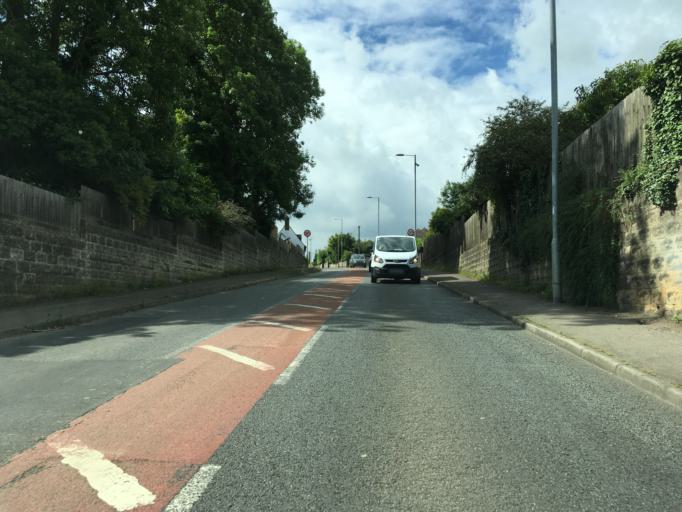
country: GB
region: England
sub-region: Borough of Swindon
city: Highworth
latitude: 51.6371
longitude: -1.7092
